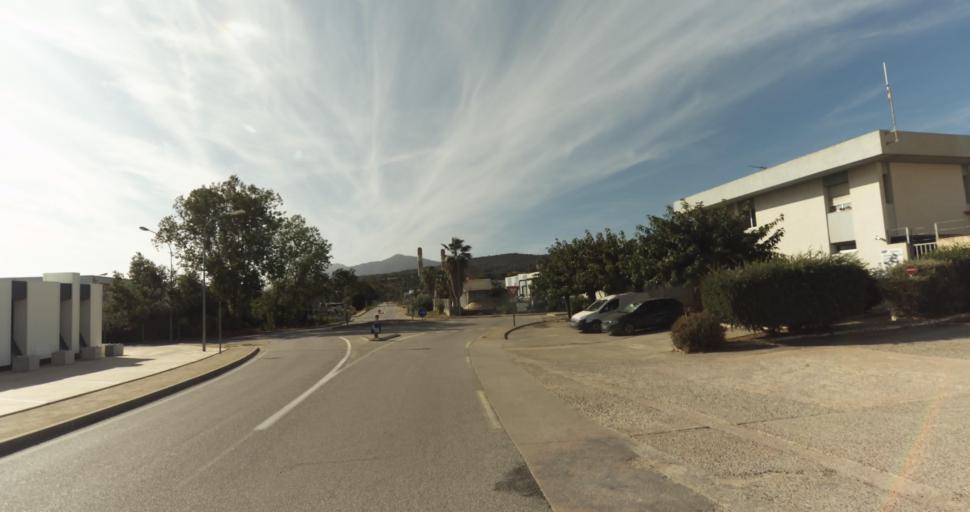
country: FR
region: Corsica
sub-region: Departement de la Corse-du-Sud
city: Afa
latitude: 41.9292
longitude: 8.7909
